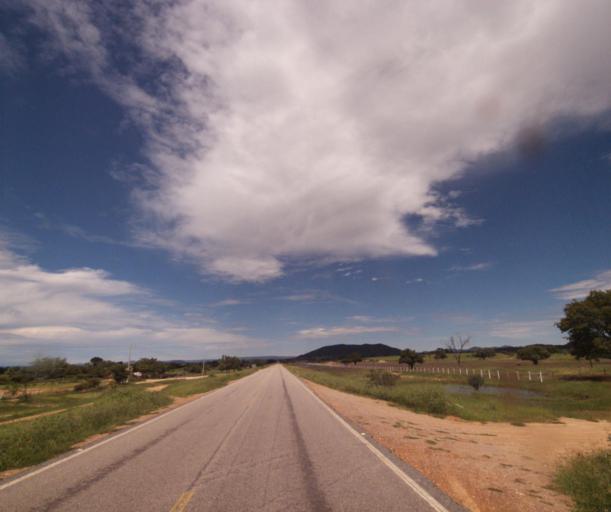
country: BR
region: Bahia
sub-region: Guanambi
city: Guanambi
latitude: -14.2292
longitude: -42.9242
